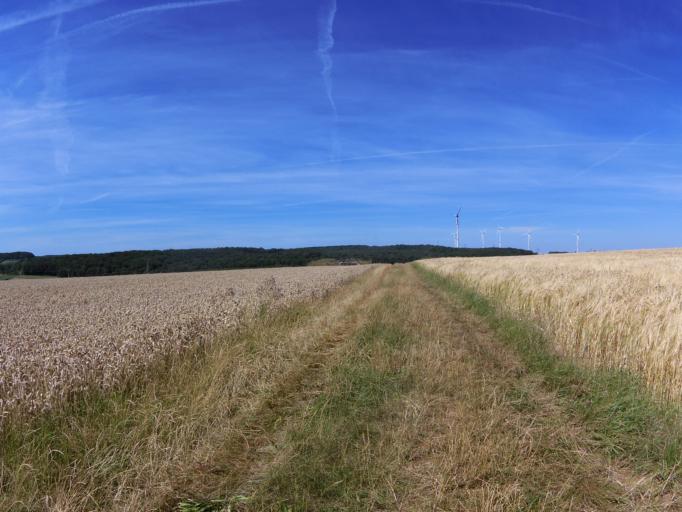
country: DE
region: Bavaria
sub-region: Regierungsbezirk Unterfranken
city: Hettstadt
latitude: 49.8089
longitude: 9.8154
